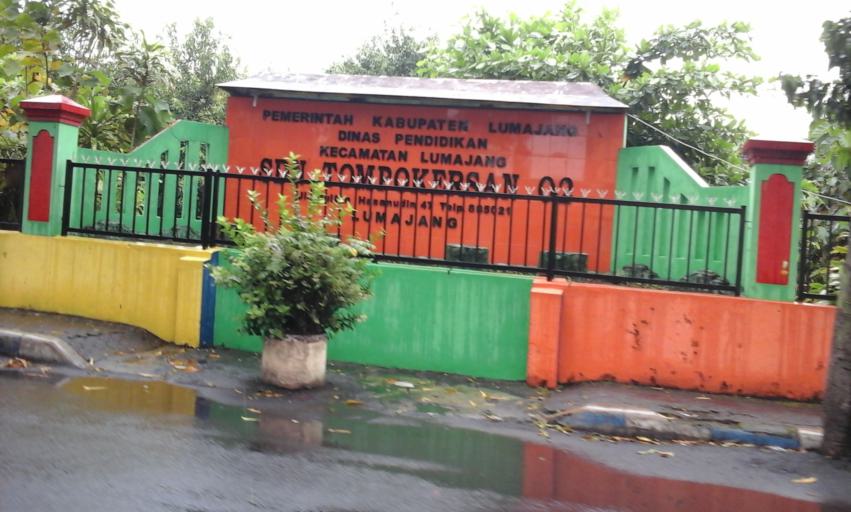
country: ID
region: East Java
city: Rogotrunan
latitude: -8.1236
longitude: 113.2304
